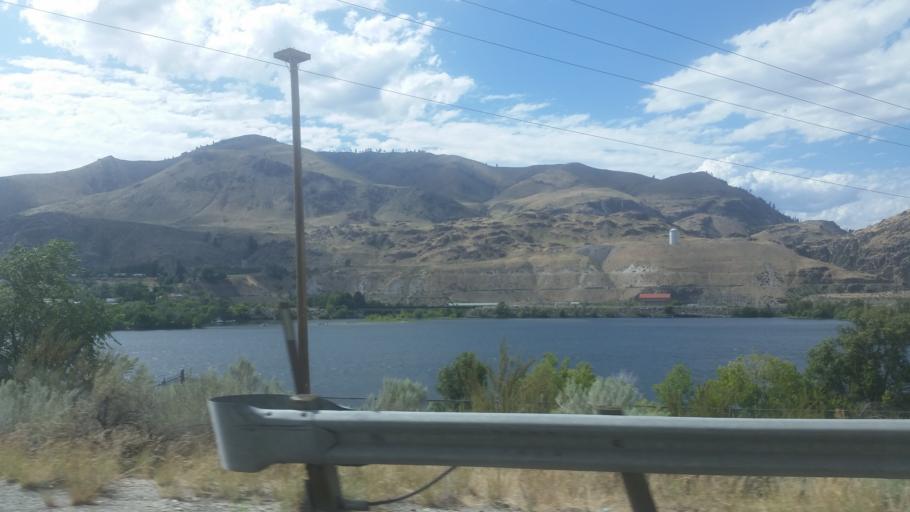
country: US
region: Washington
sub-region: Chelan County
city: Chelan
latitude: 47.8026
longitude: -119.9746
